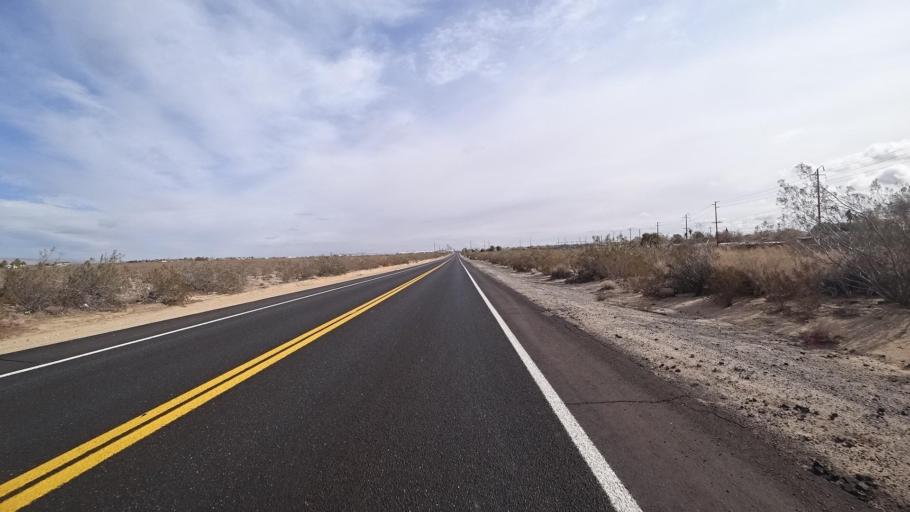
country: US
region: California
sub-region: Kern County
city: Mojave
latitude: 35.0535
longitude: -118.1911
